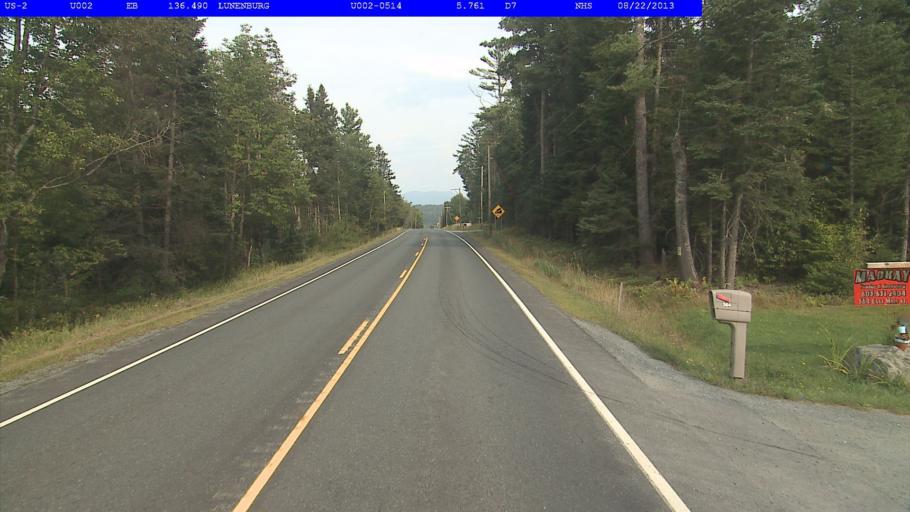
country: US
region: New Hampshire
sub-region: Coos County
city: Lancaster
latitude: 44.4644
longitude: -71.6609
